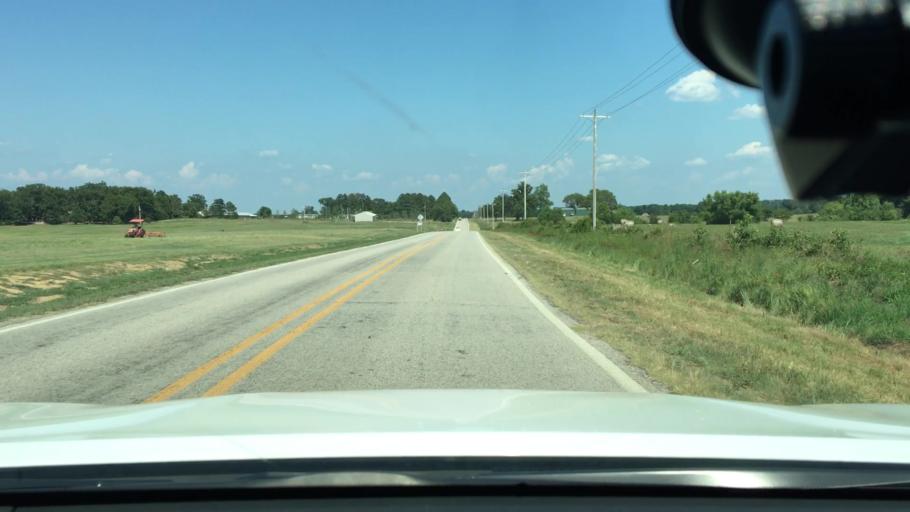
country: US
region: Arkansas
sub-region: Johnson County
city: Coal Hill
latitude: 35.3512
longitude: -93.5871
